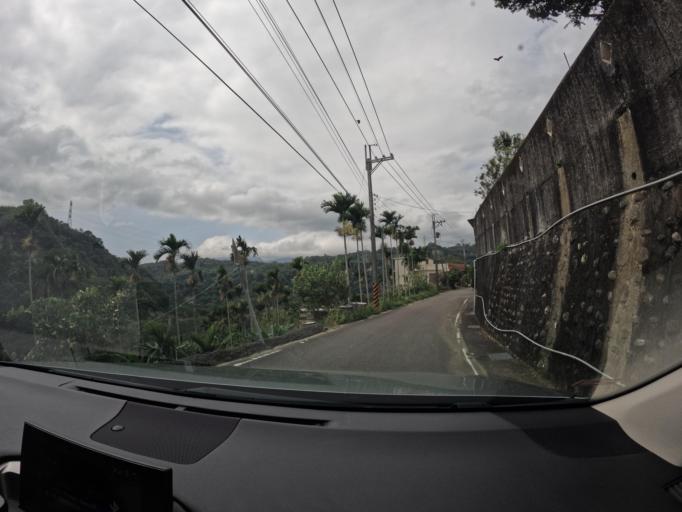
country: TW
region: Taiwan
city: Fengyuan
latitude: 24.3492
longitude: 120.8730
